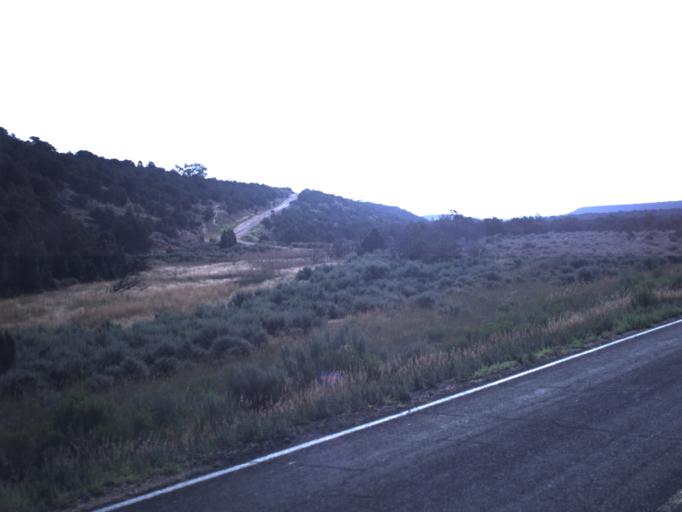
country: US
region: Utah
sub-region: Duchesne County
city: Duchesne
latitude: 40.3235
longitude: -110.4025
